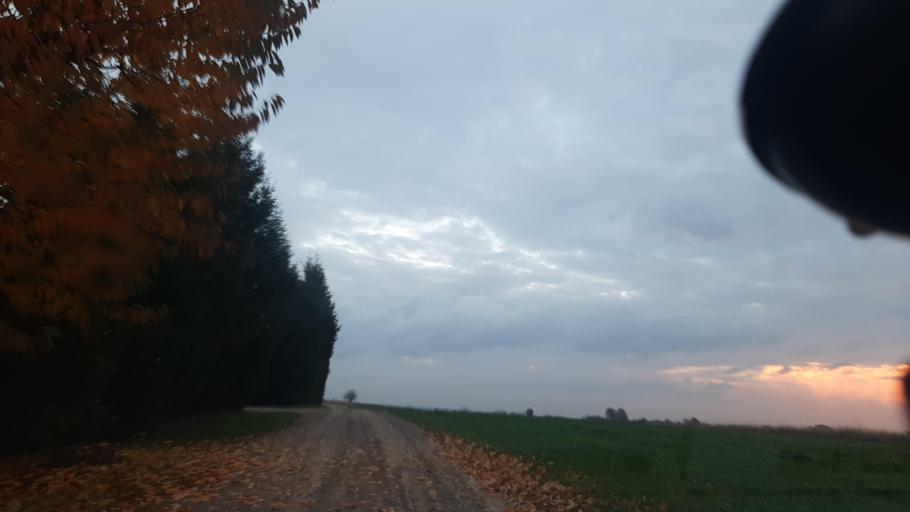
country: PL
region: Lublin Voivodeship
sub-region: Powiat lubelski
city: Jastkow
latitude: 51.3313
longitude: 22.3923
